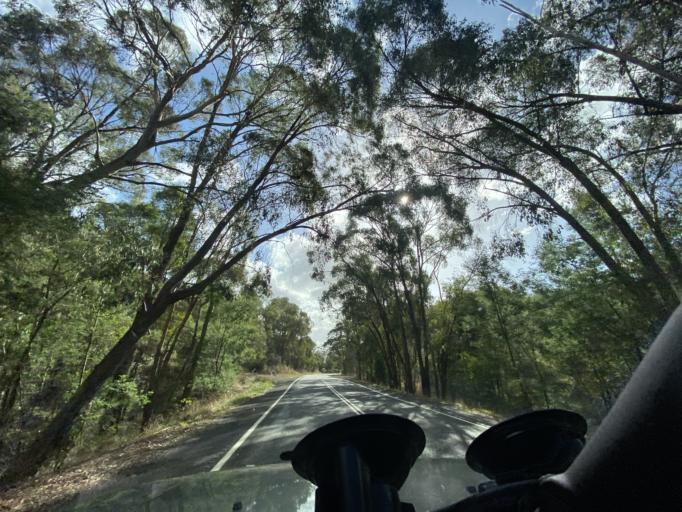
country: AU
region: Victoria
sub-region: Murrindindi
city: Kinglake West
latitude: -37.3276
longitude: 145.3286
